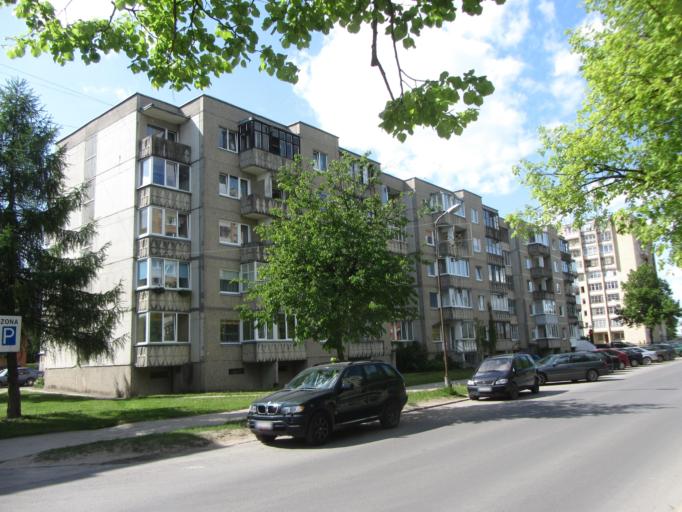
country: LT
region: Utenos apskritis
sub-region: Utena
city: Utena
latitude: 55.5084
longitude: 25.5847
